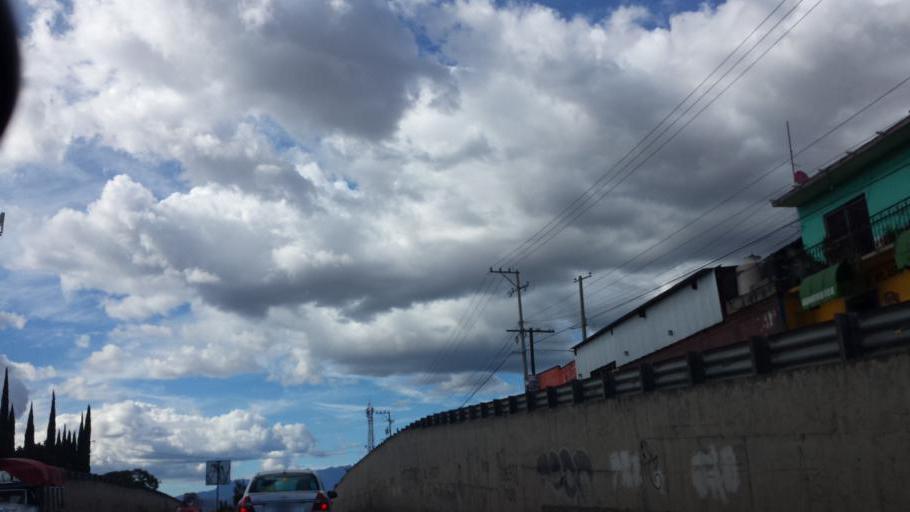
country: MX
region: Oaxaca
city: Tlacolula de Matamoros
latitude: 16.9579
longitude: -96.4734
